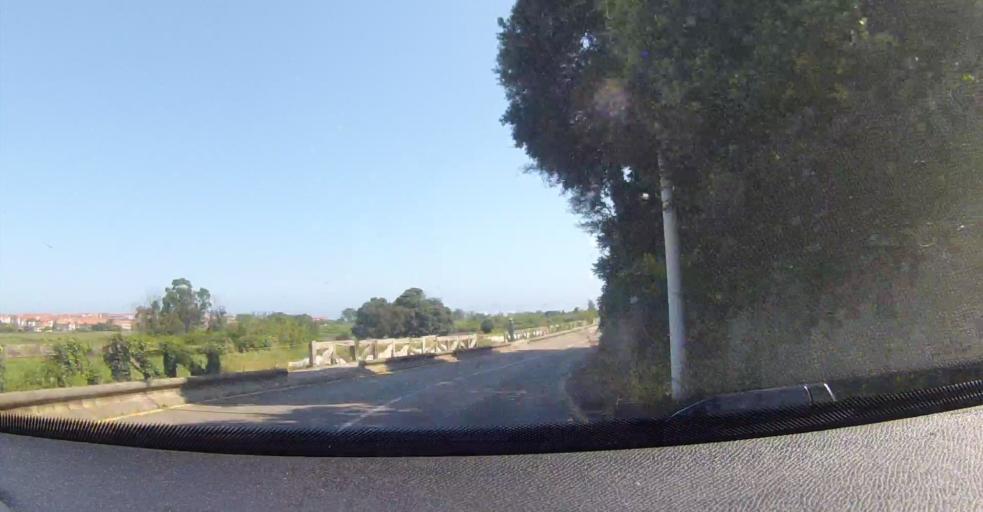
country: ES
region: Cantabria
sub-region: Provincia de Cantabria
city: Noja
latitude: 43.4683
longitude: -3.5169
